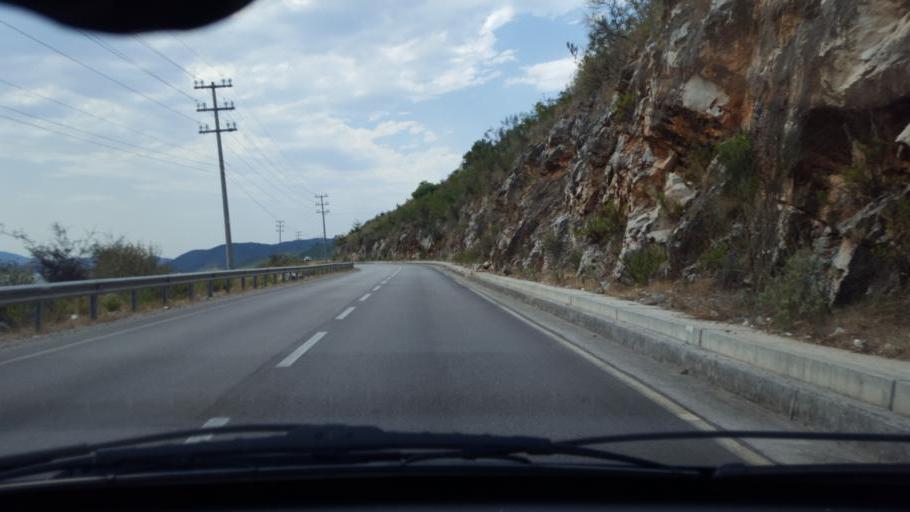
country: AL
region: Vlore
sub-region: Rrethi i Sarandes
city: Sarande
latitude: 39.8014
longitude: 20.0119
